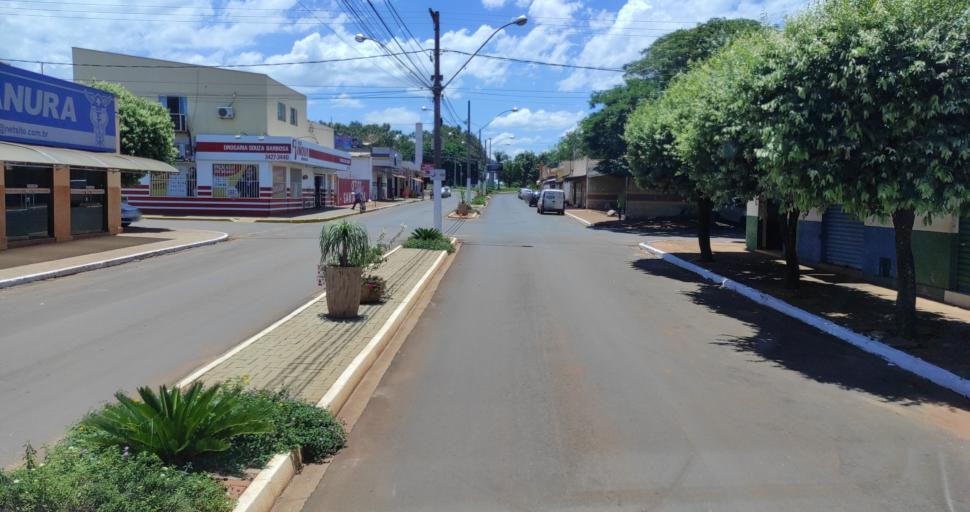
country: BR
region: Minas Gerais
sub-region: Frutal
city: Frutal
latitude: -20.1377
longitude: -48.7008
